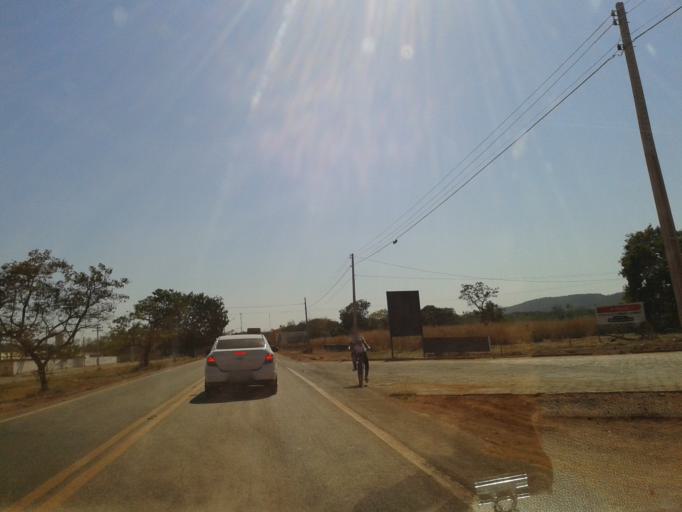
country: BR
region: Goias
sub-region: Crixas
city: Crixas
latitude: -14.1102
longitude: -50.3419
